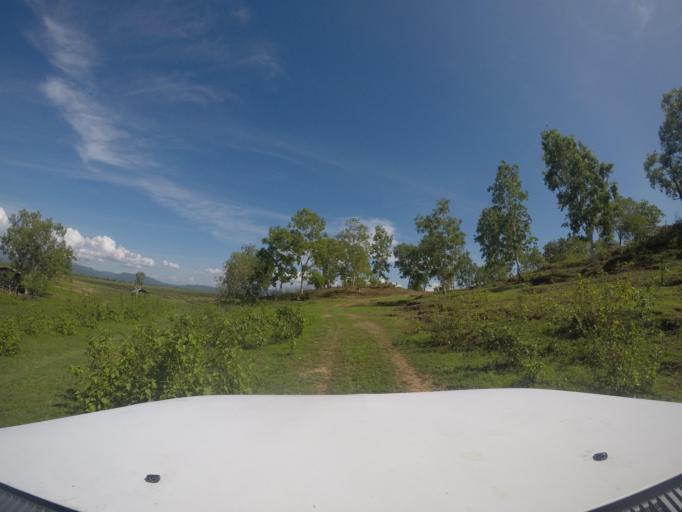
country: TL
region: Bobonaro
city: Maliana
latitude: -8.9798
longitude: 125.1939
